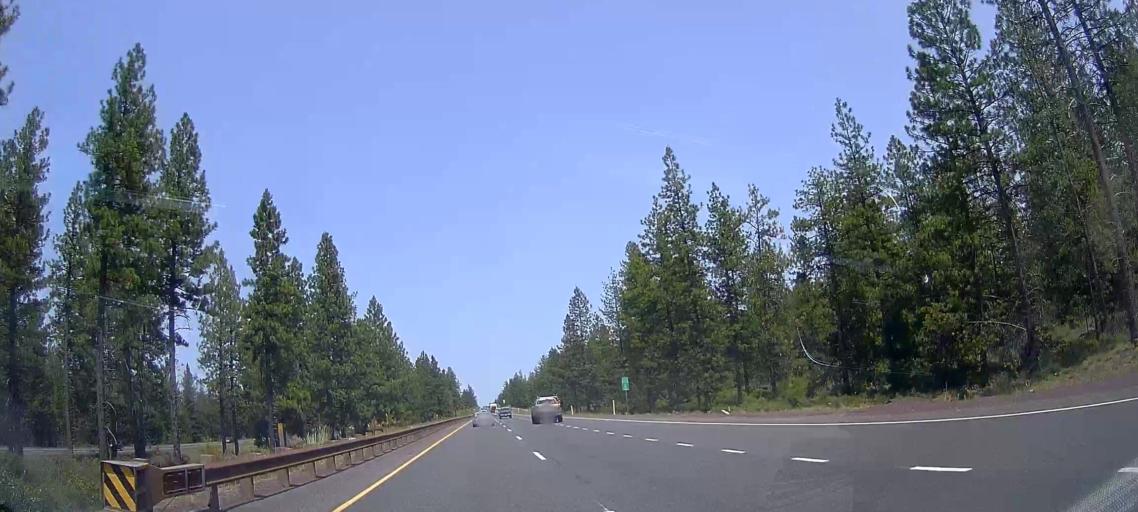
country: US
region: Oregon
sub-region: Deschutes County
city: Sunriver
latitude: 43.8930
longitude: -121.3756
